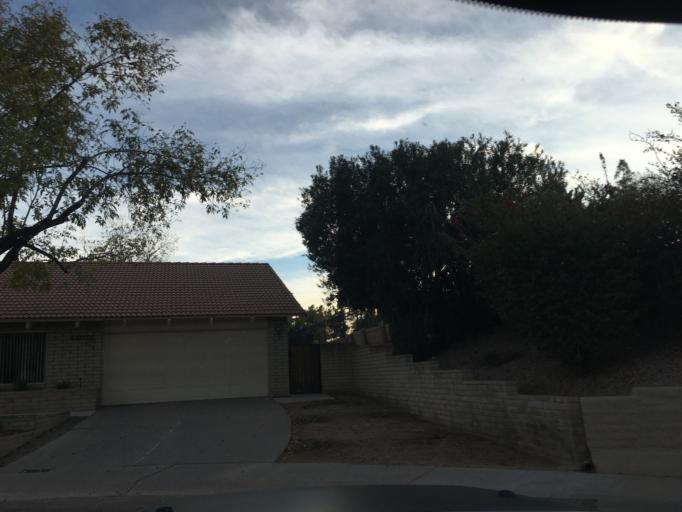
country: US
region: Arizona
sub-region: Maricopa County
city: Tempe
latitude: 33.3762
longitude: -111.9189
